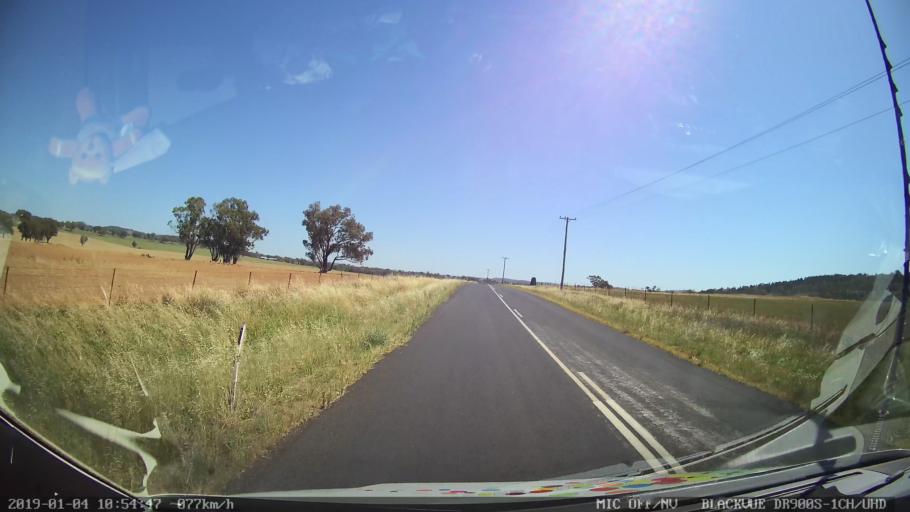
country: AU
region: New South Wales
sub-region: Cabonne
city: Molong
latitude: -33.2010
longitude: 148.6904
